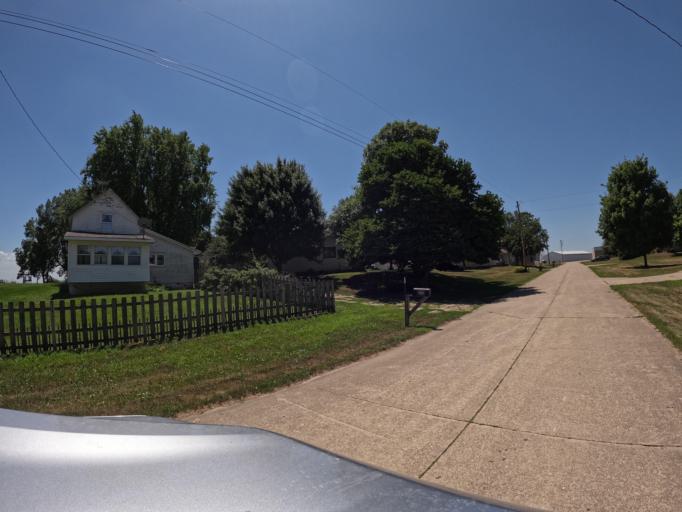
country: US
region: Iowa
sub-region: Poweshiek County
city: Montezuma
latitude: 41.4802
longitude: -92.3917
